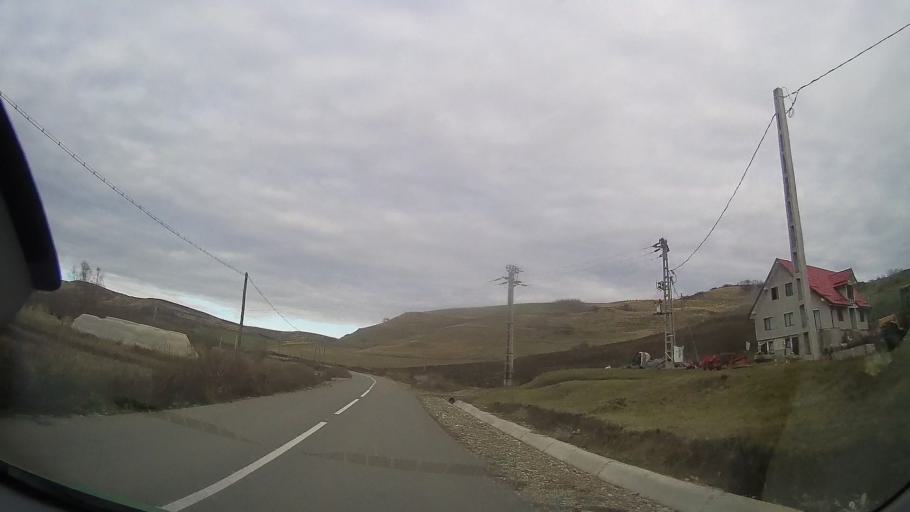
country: RO
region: Bistrita-Nasaud
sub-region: Comuna Silvasu de Campie
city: Silvasu de Campie
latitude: 46.8146
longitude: 24.2972
